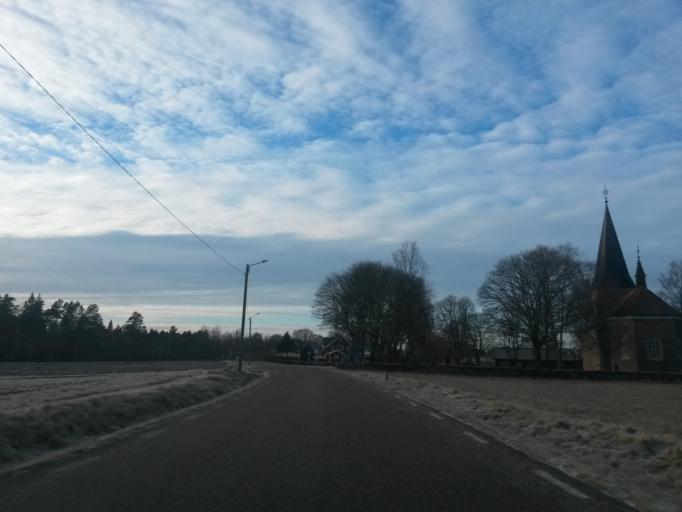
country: SE
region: Vaestra Goetaland
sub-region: Boras Kommun
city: Boras
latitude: 57.8587
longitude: 12.9332
